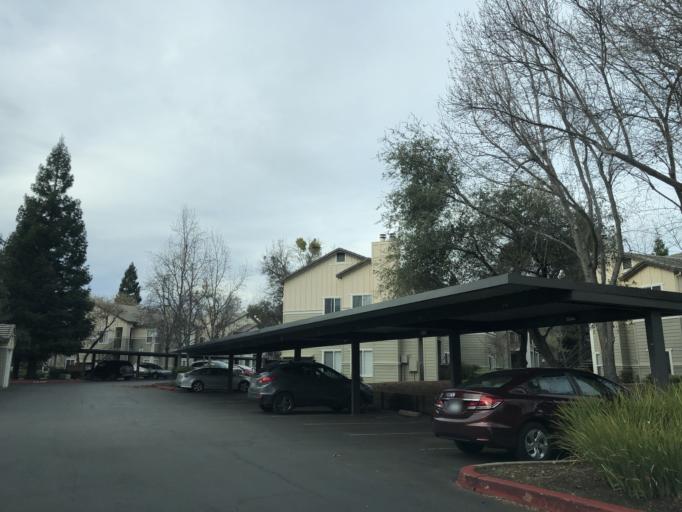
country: US
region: California
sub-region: Sacramento County
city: Folsom
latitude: 38.6491
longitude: -121.1808
